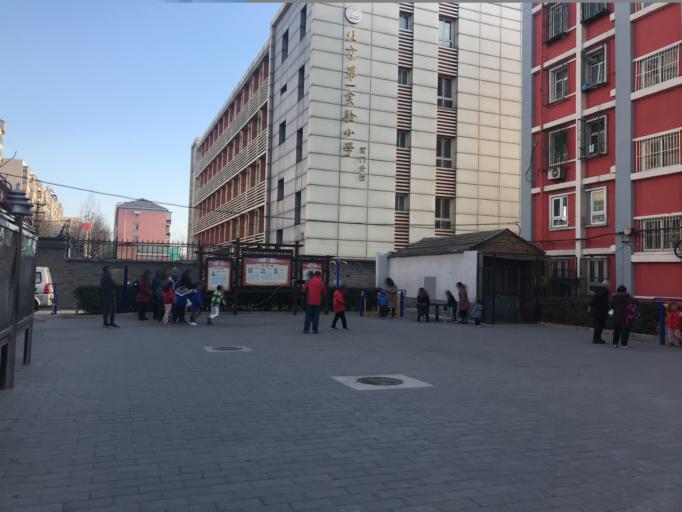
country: CN
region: Beijing
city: Beijing
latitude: 39.8981
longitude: 116.3817
